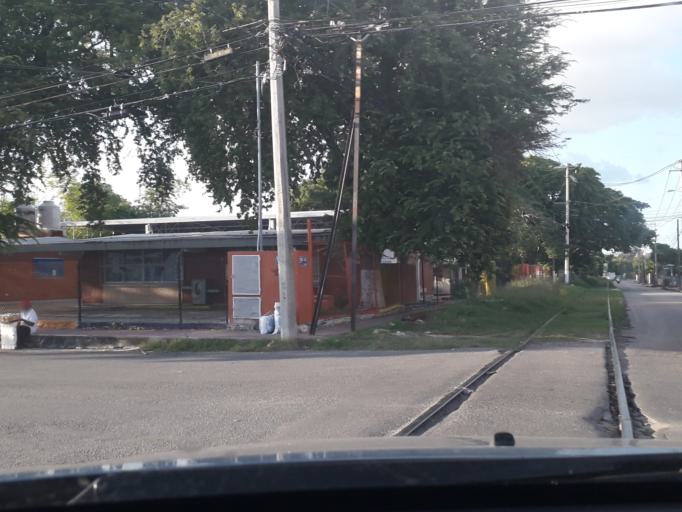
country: MX
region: Yucatan
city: Merida
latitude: 20.9664
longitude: -89.6439
